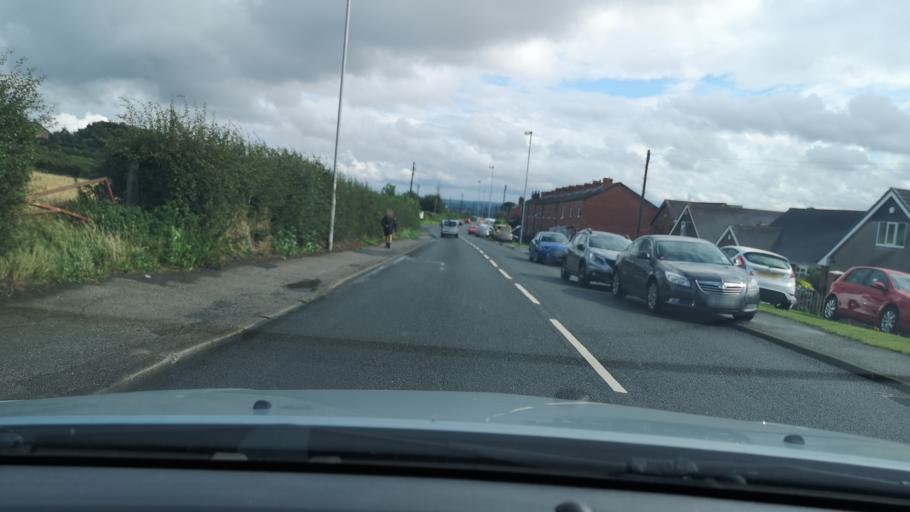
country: GB
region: England
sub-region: City and Borough of Wakefield
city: Ossett
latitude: 53.6985
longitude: -1.5499
